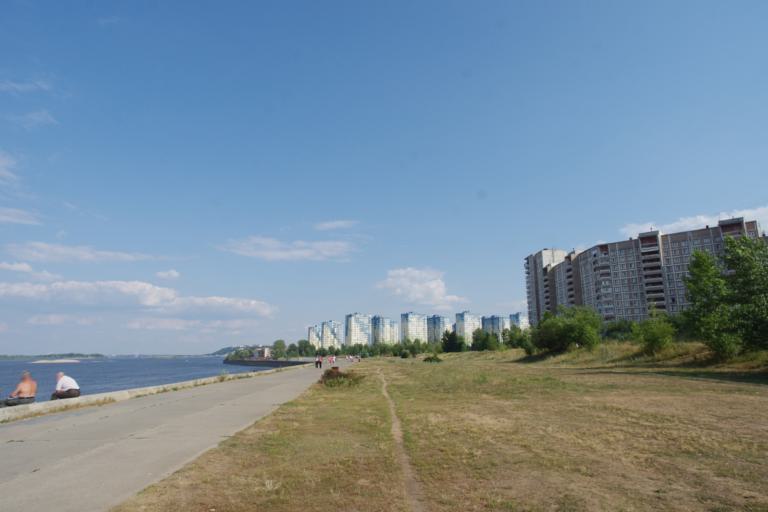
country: RU
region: Nizjnij Novgorod
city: Nizhniy Novgorod
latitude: 56.3458
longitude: 43.9422
